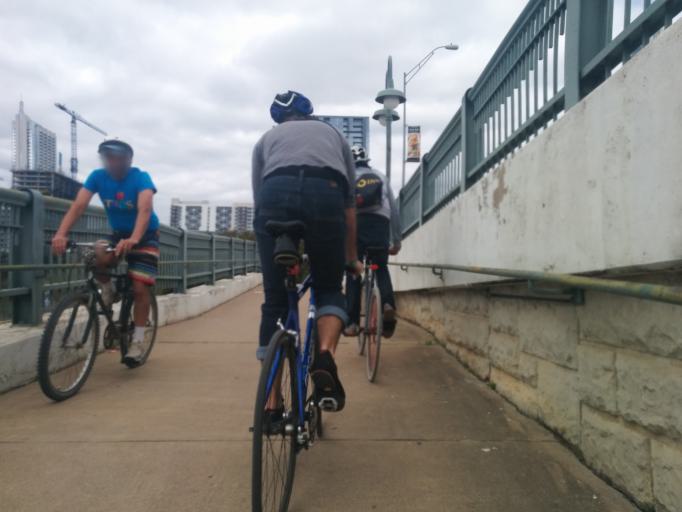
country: US
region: Texas
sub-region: Travis County
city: Austin
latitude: 30.2611
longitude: -97.7488
